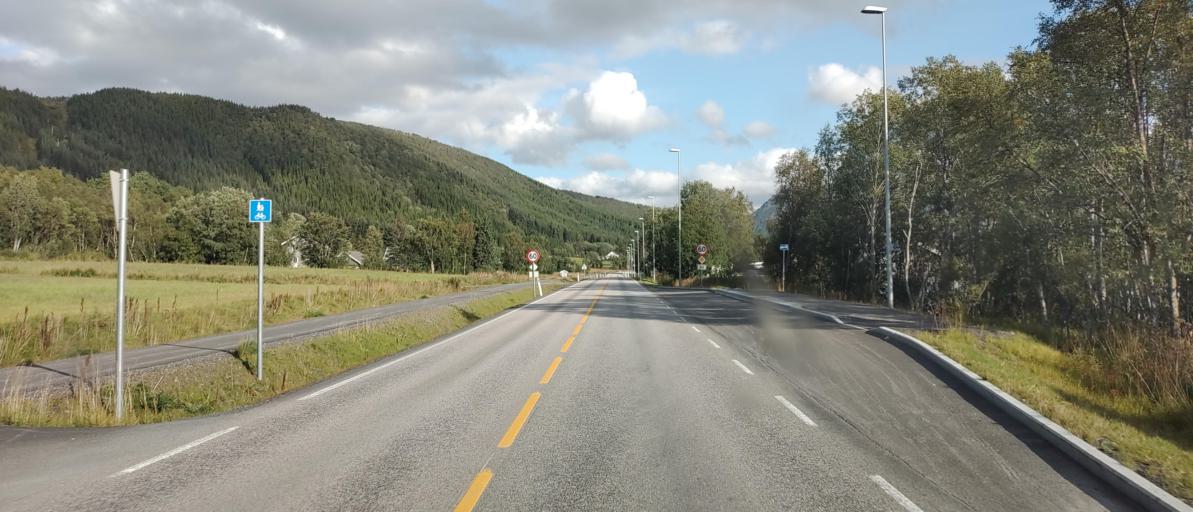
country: NO
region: Nordland
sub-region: Sortland
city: Sortland
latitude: 68.7516
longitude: 15.4798
